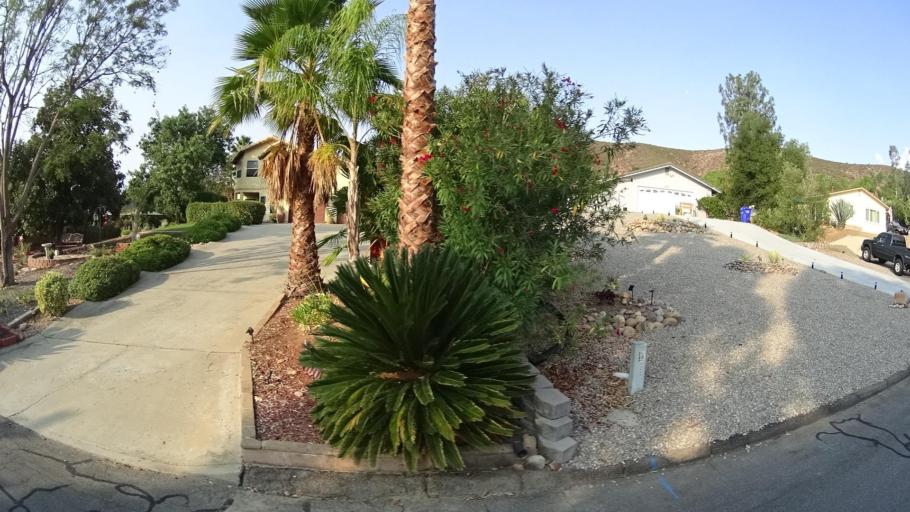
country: US
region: California
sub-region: San Diego County
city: San Diego Country Estates
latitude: 33.0124
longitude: -116.8246
